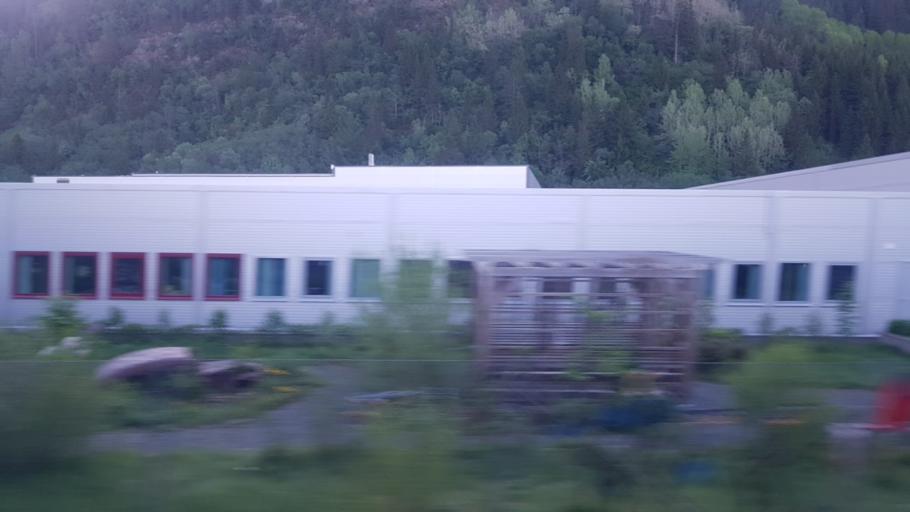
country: NO
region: Sor-Trondelag
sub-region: Melhus
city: Melhus
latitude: 63.2545
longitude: 10.2811
